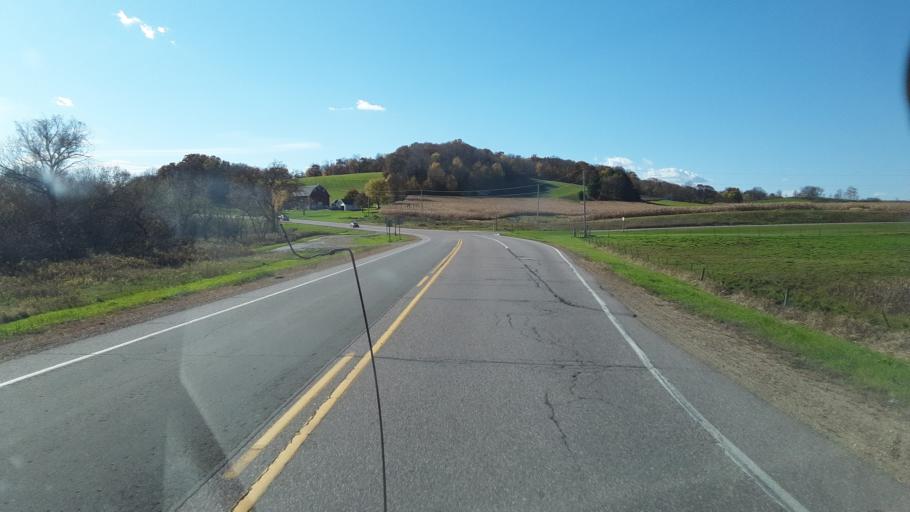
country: US
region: Wisconsin
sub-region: Sauk County
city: Reedsburg
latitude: 43.5407
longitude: -90.1709
